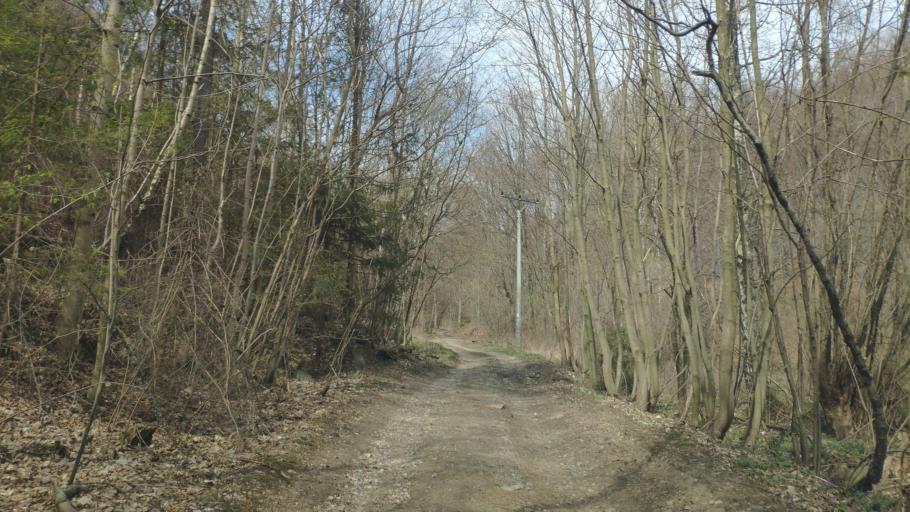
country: SK
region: Kosicky
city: Moldava nad Bodvou
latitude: 48.7495
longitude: 21.0276
